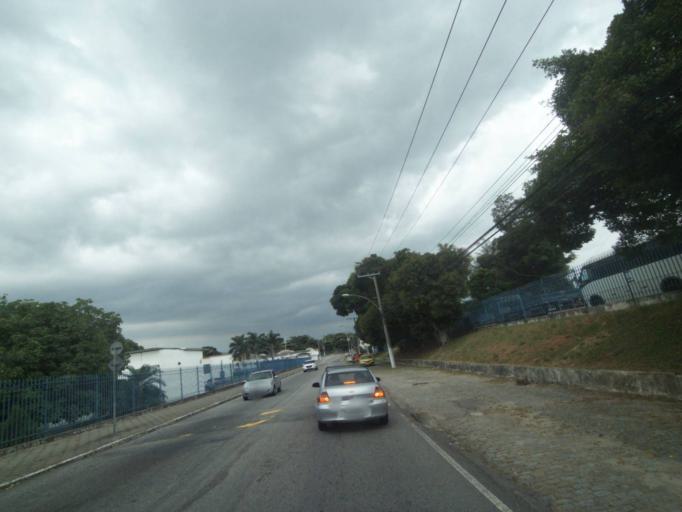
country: BR
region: Rio de Janeiro
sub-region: Sao Joao De Meriti
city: Sao Joao de Meriti
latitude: -22.8808
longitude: -43.3817
